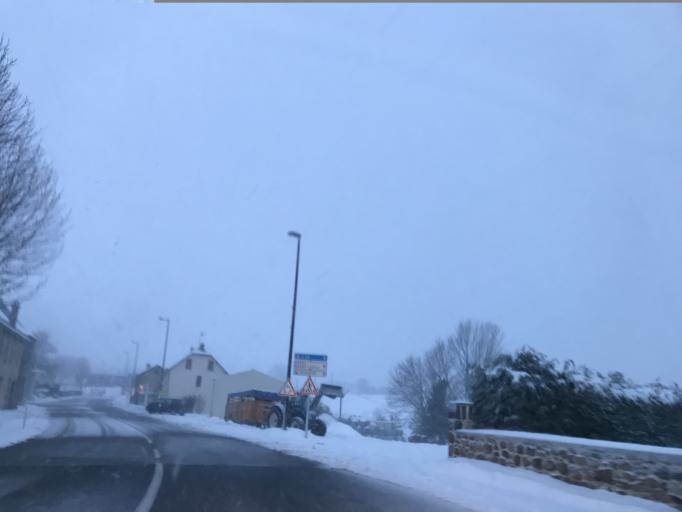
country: FR
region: Auvergne
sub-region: Departement du Puy-de-Dome
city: Saint-Sauves-d'Auvergne
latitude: 45.6489
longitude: 2.7080
